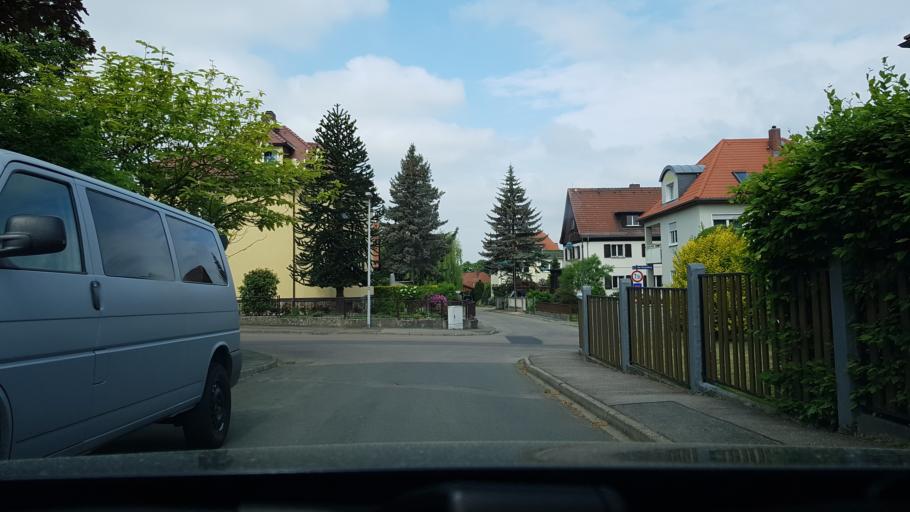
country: DE
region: Saxony
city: Bannewitz
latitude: 51.0294
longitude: 13.6951
